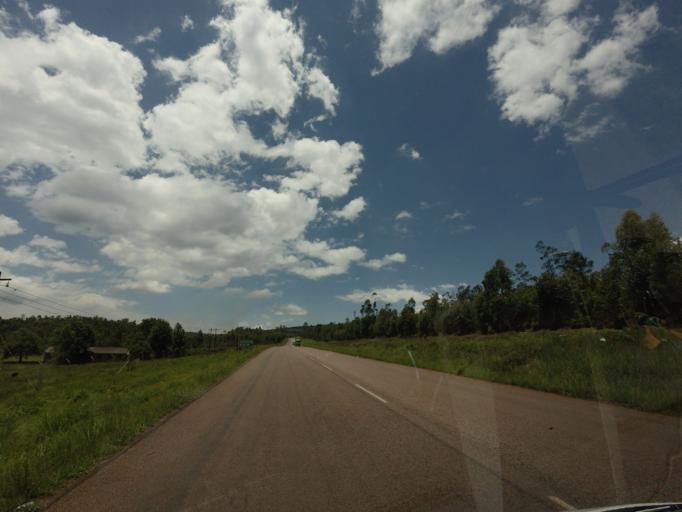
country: ZA
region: Mpumalanga
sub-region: Ehlanzeni District
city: Graksop
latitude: -25.0801
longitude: 30.7928
